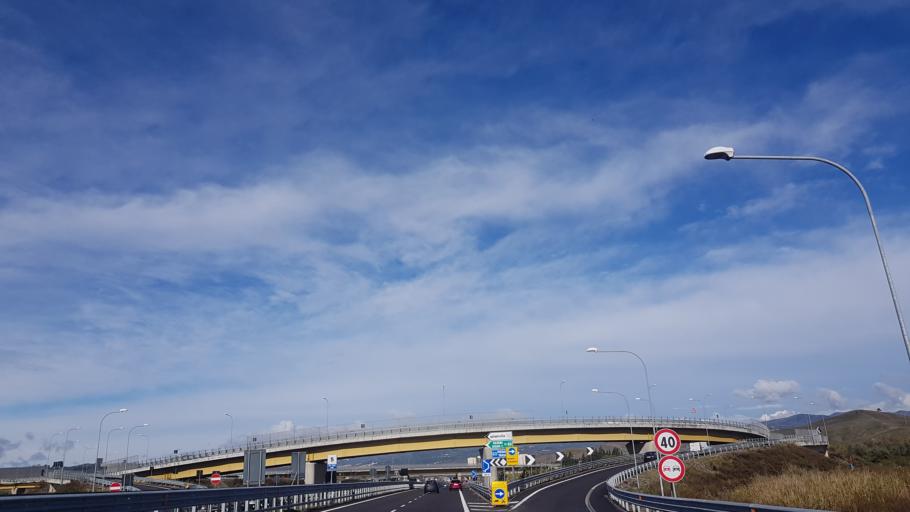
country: IT
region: Calabria
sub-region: Provincia di Catanzaro
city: Catanzaro
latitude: 38.8487
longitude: 16.5801
